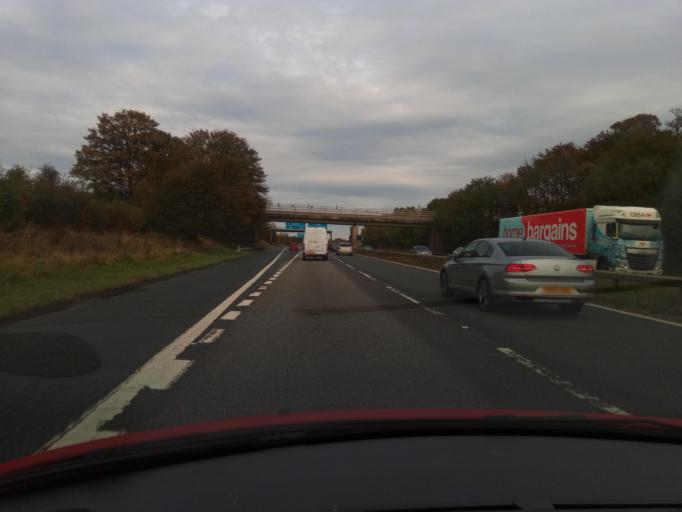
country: GB
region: England
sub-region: Darlington
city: High Coniscliffe
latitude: 54.4922
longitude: -1.6329
